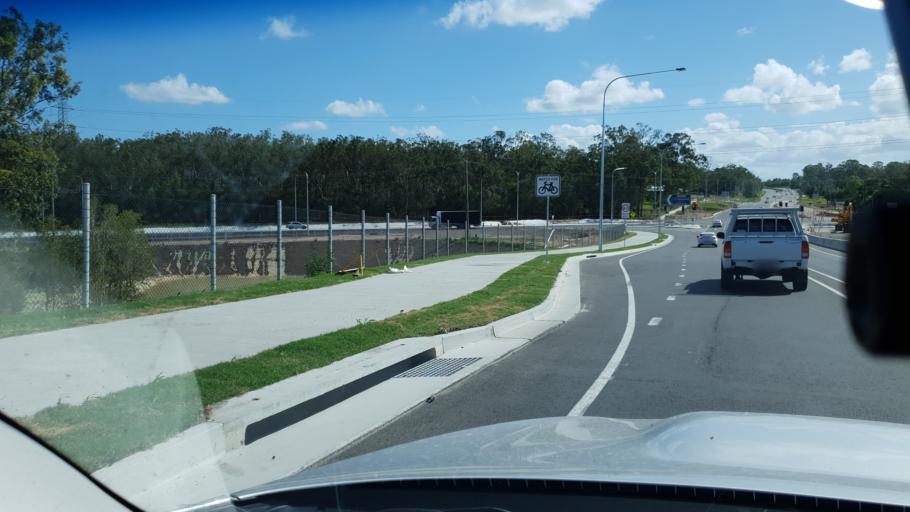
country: AU
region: Queensland
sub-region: Logan
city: Woodridge
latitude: -27.6529
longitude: 153.0698
